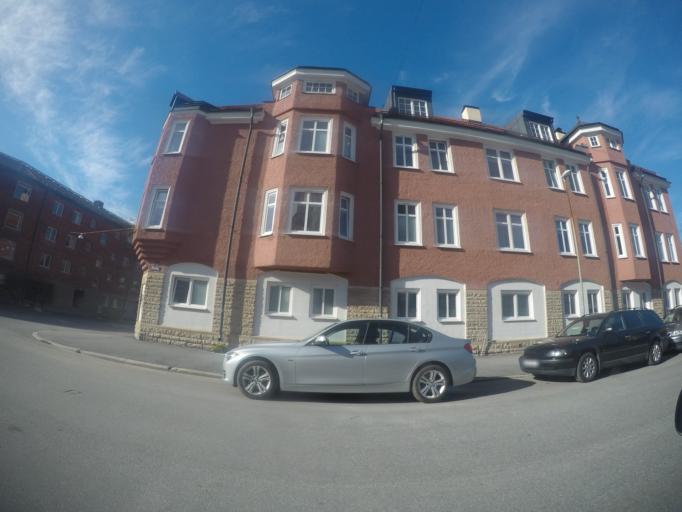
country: SE
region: OErebro
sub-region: Orebro Kommun
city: Orebro
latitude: 59.2825
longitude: 15.2299
